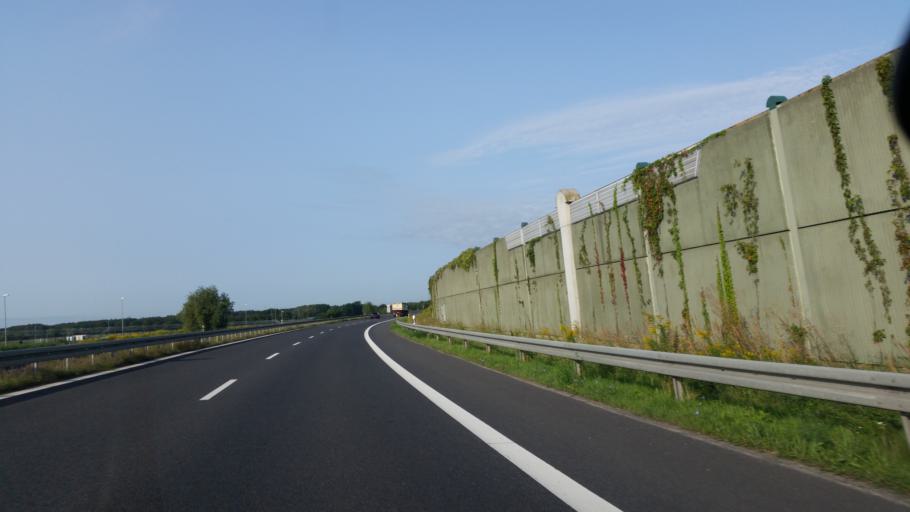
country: DE
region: Brandenburg
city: Schonefeld
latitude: 52.3696
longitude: 13.4796
